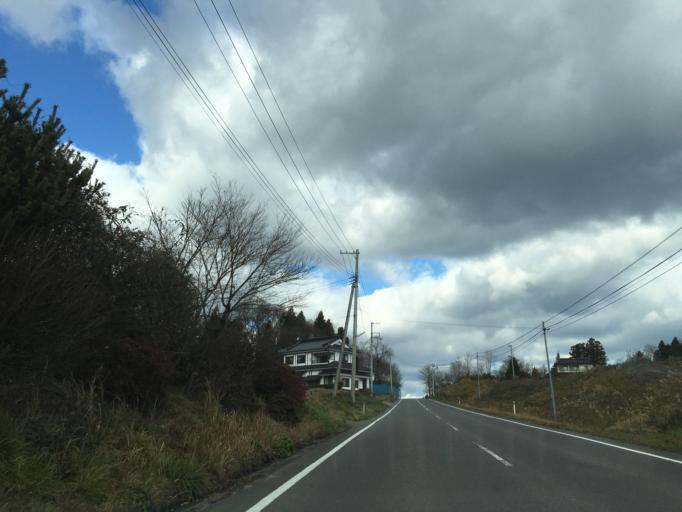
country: JP
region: Fukushima
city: Sukagawa
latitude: 37.3249
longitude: 140.4402
